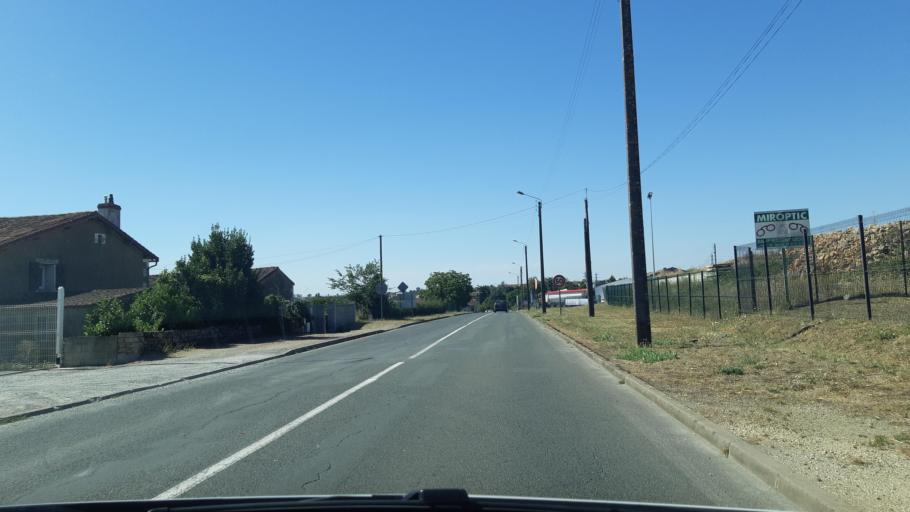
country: FR
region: Poitou-Charentes
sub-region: Departement des Deux-Sevres
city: Exireuil
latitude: 46.4233
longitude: -0.2057
